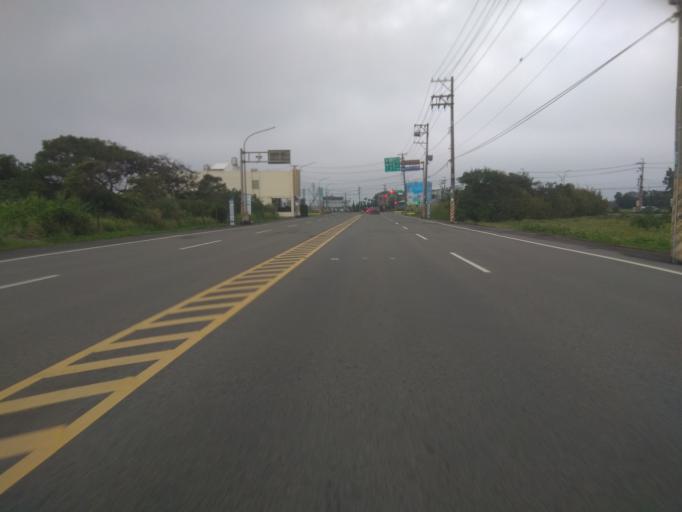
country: TW
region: Taiwan
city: Taoyuan City
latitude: 25.0331
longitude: 121.0964
